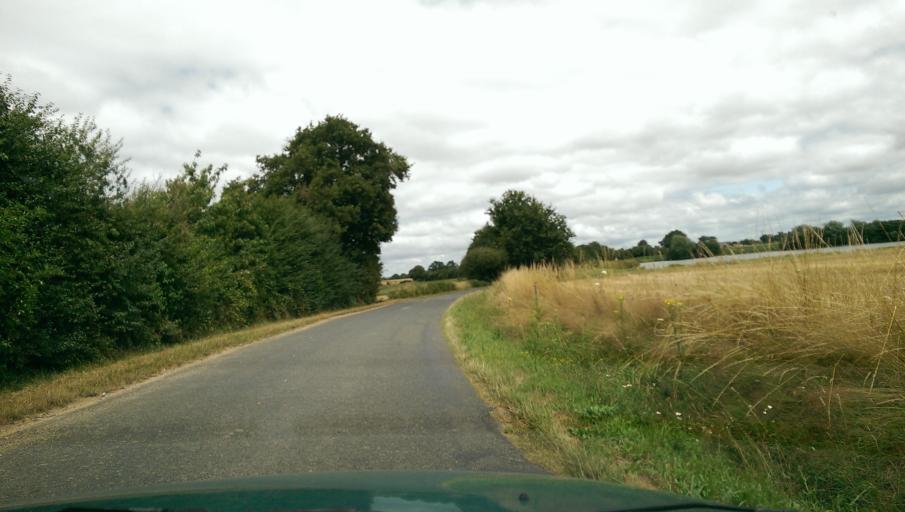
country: FR
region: Pays de la Loire
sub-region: Departement de la Loire-Atlantique
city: Vieillevigne
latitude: 46.9874
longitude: -1.4231
